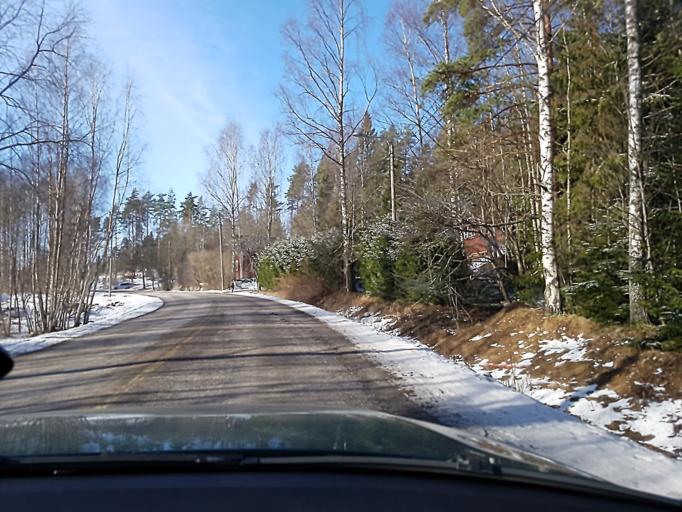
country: FI
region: Uusimaa
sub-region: Helsinki
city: Kirkkonummi
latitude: 60.1227
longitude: 24.3908
